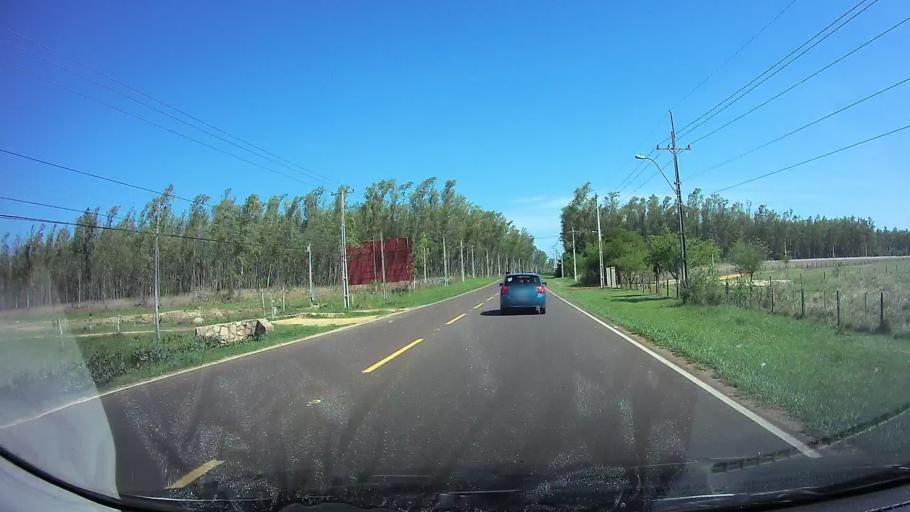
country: PY
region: Central
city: Ypacarai
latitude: -25.3729
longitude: -57.2632
